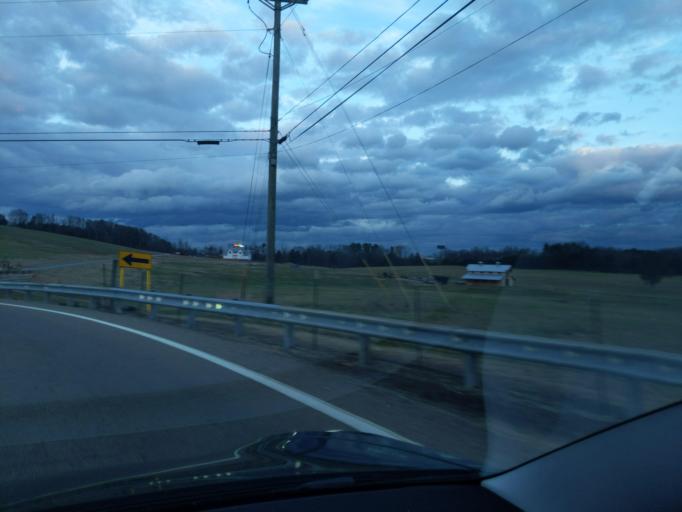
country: US
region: Tennessee
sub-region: Jefferson County
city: White Pine
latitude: 36.1037
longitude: -83.3475
